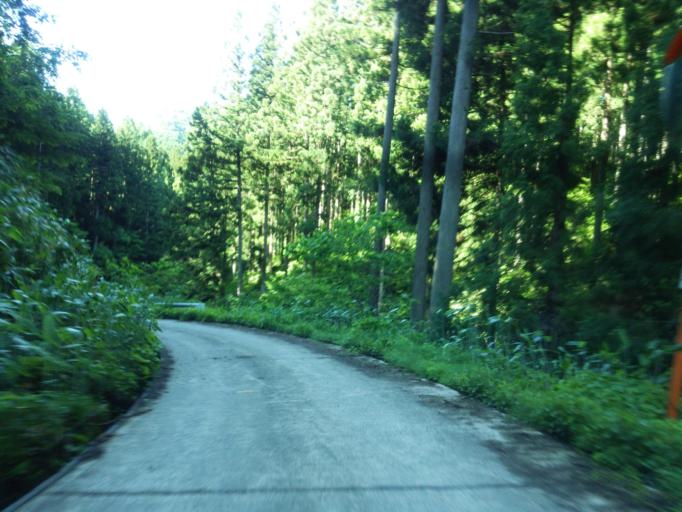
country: JP
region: Fukushima
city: Kitakata
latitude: 37.3828
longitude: 139.8244
